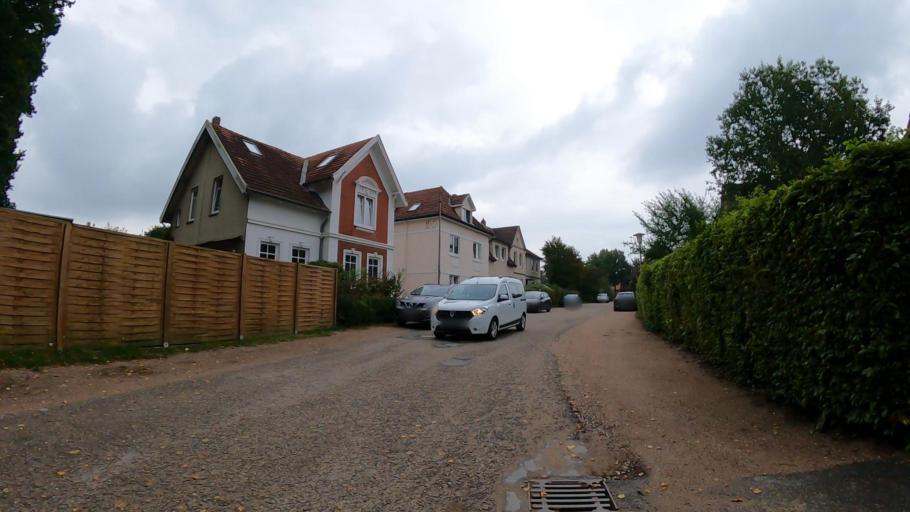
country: DE
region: Schleswig-Holstein
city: Rellingen
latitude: 53.6415
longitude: 9.8153
